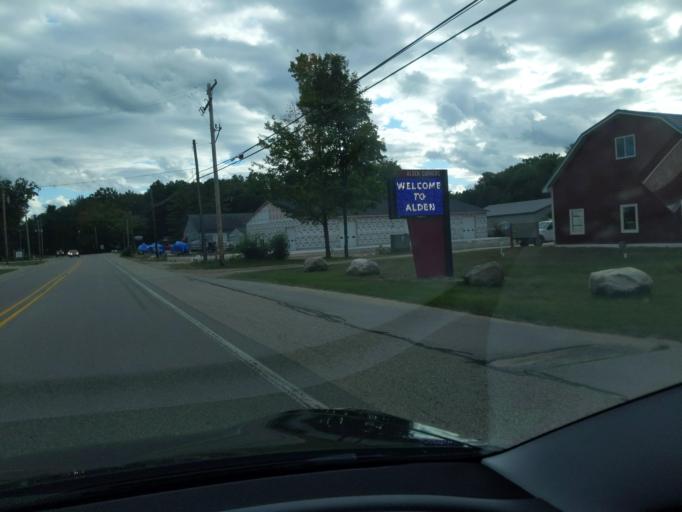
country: US
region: Michigan
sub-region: Kalkaska County
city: Rapid City
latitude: 44.8610
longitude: -85.2822
